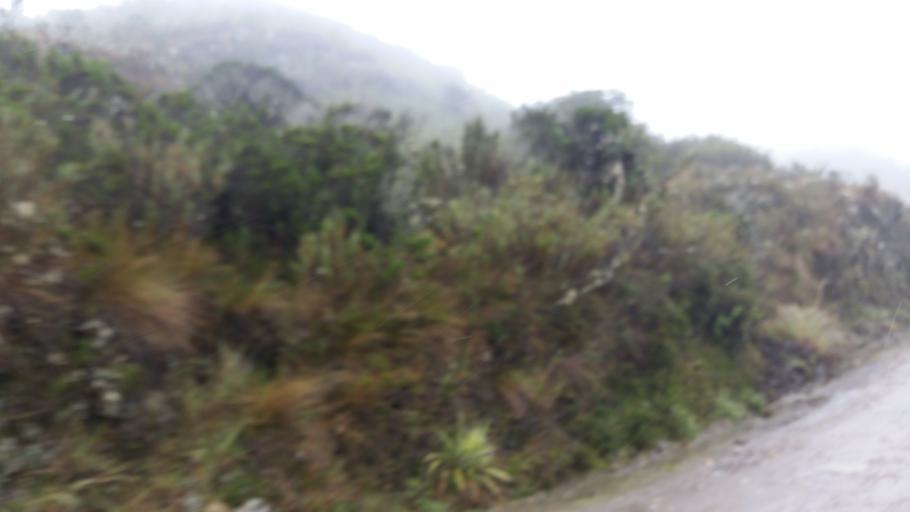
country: CO
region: Cundinamarca
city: La Calera
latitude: 4.6969
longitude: -73.8020
